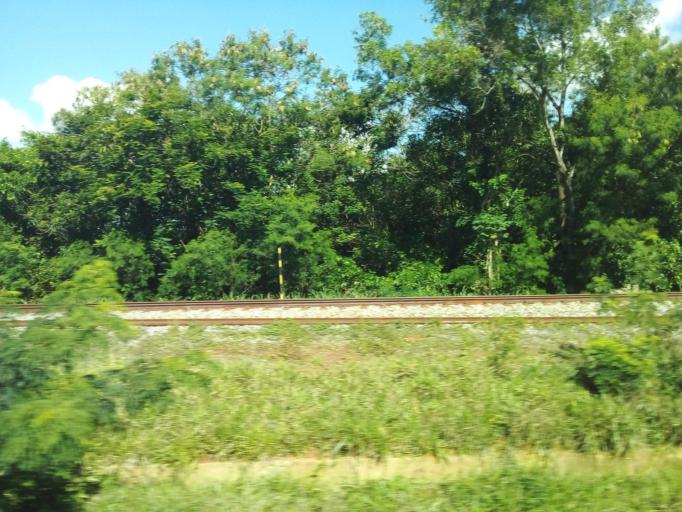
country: BR
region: Minas Gerais
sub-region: Governador Valadares
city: Governador Valadares
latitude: -18.8570
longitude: -41.8629
